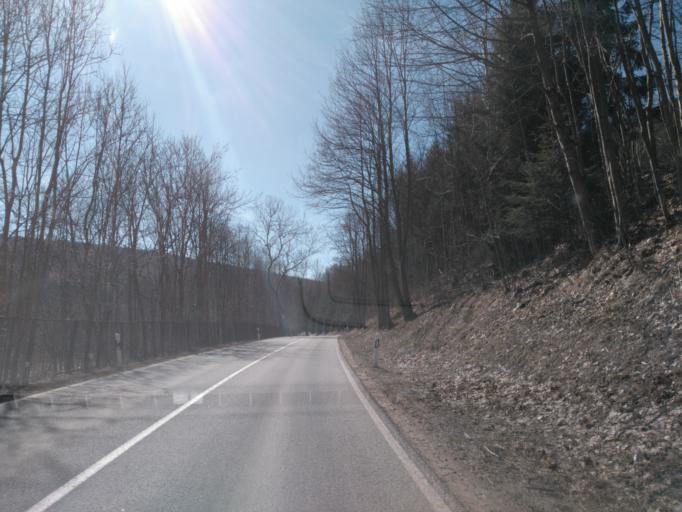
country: CZ
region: Ustecky
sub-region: Okres Chomutov
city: Vejprty
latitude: 50.4567
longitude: 13.0212
